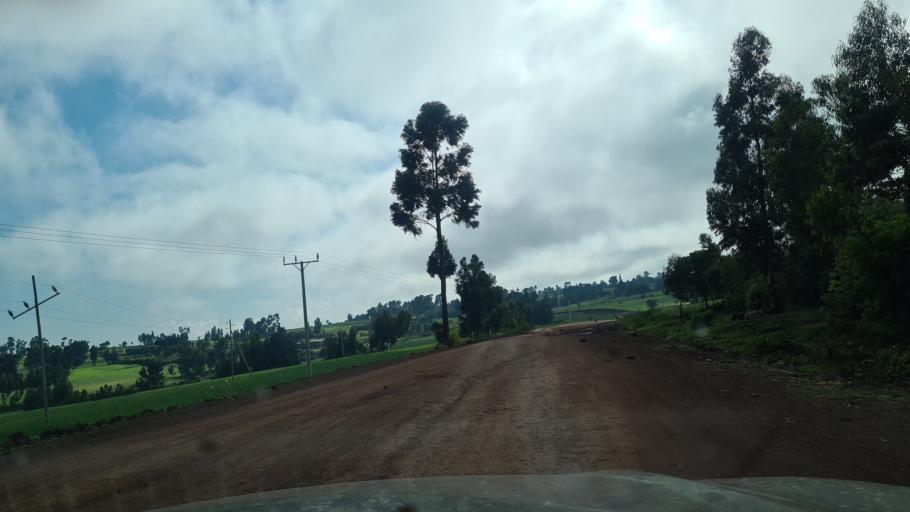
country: ET
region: Oromiya
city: Huruta
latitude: 8.1247
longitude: 39.3715
